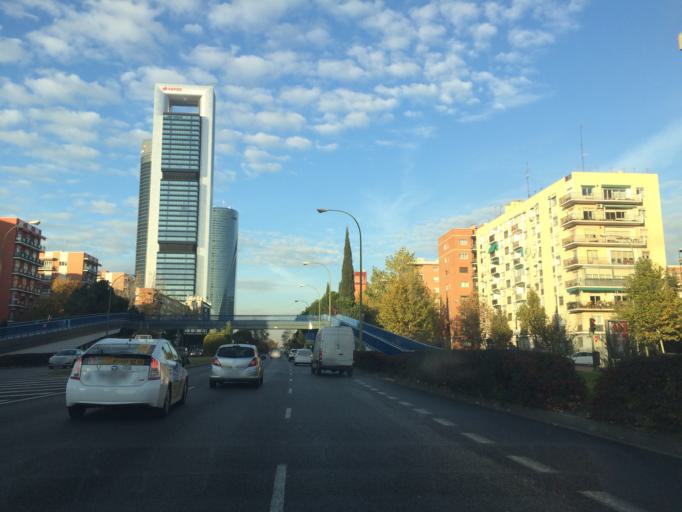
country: ES
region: Madrid
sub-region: Provincia de Madrid
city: Chamartin
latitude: 40.4706
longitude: -3.6880
